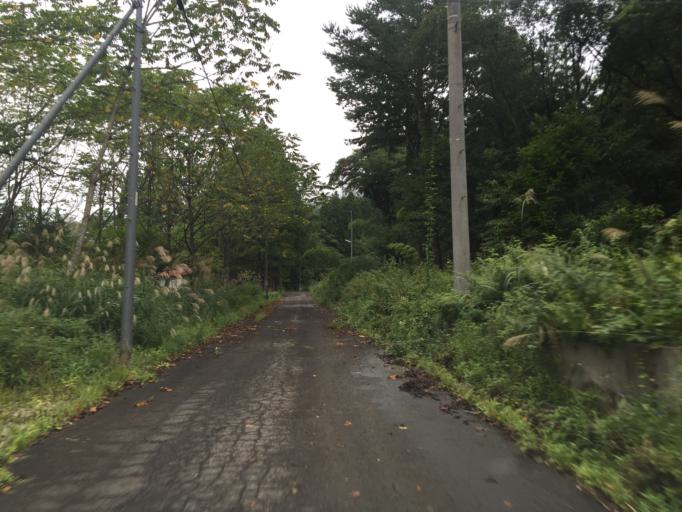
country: JP
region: Fukushima
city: Fukushima-shi
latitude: 37.8092
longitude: 140.3397
